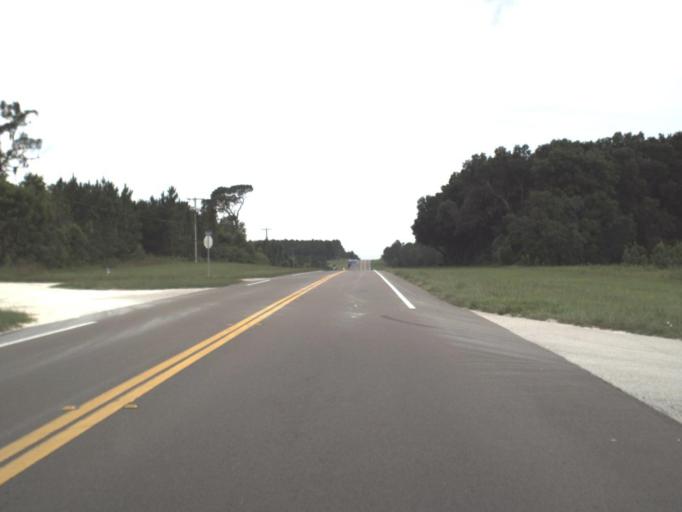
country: US
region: Florida
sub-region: Pasco County
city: Zephyrhills North
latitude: 28.3101
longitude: -82.1668
